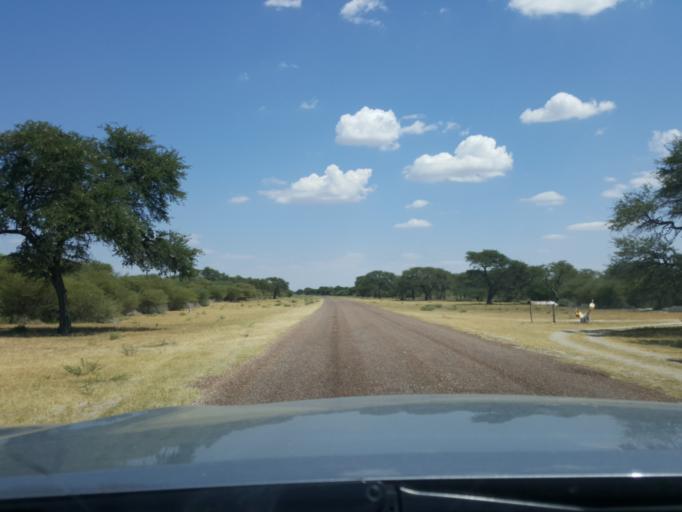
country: BW
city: Sehithwa
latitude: -20.3784
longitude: 22.8216
